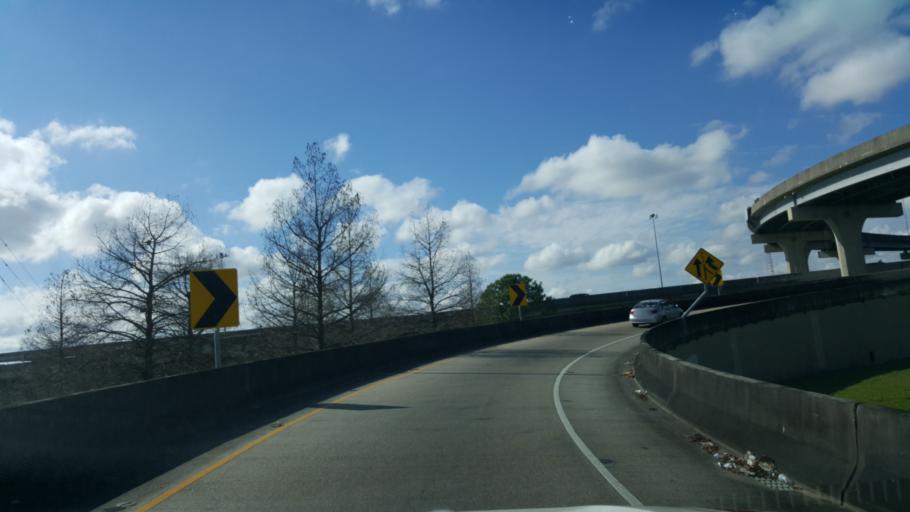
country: US
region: Louisiana
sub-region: Jefferson Parish
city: Terrytown
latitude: 29.9293
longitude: -90.0368
